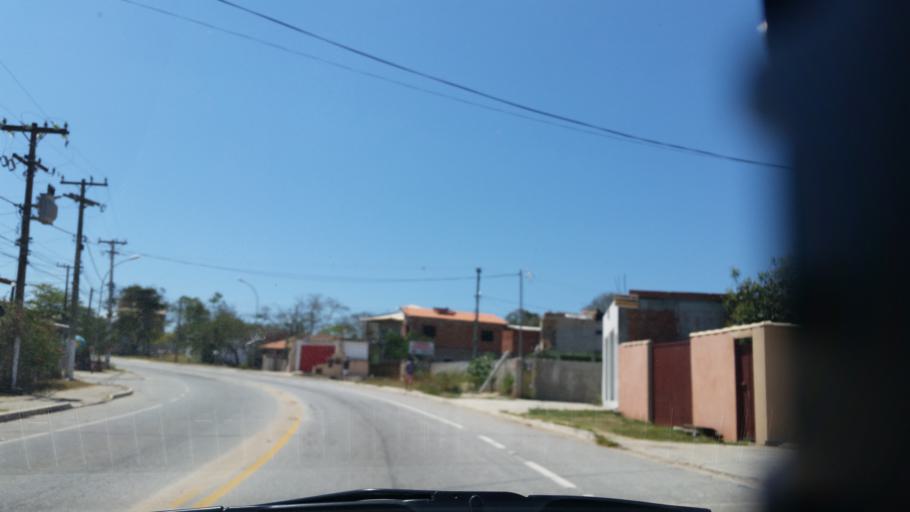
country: BR
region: Rio de Janeiro
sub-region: Cabo Frio
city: Cabo Frio
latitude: -22.8120
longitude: -41.9759
